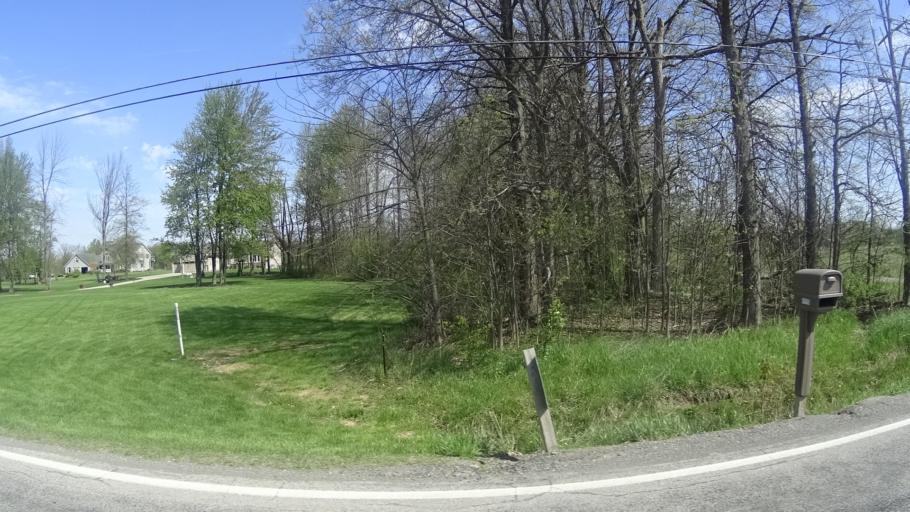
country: US
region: Ohio
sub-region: Lorain County
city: Lagrange
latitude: 41.2747
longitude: -82.1246
